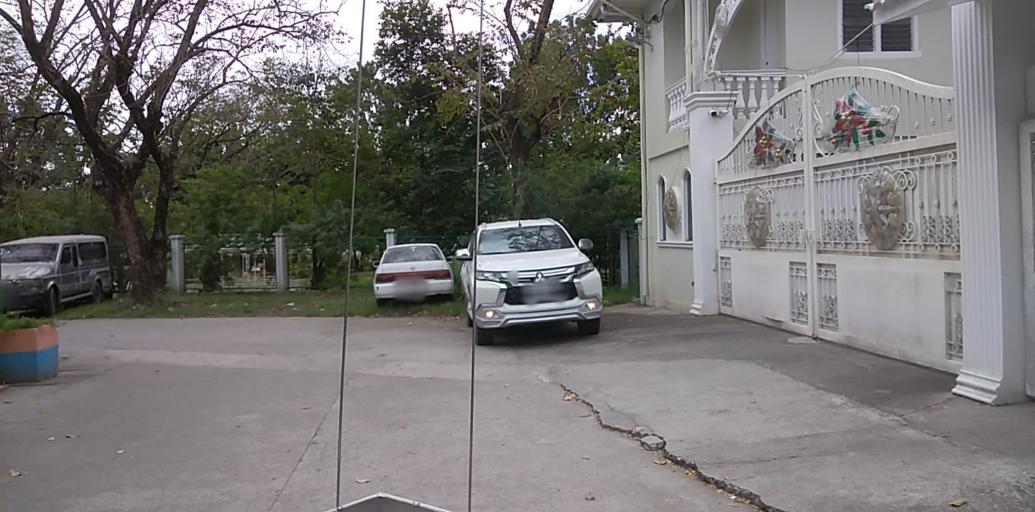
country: PH
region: Central Luzon
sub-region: Province of Pampanga
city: Porac
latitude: 15.0713
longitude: 120.5390
